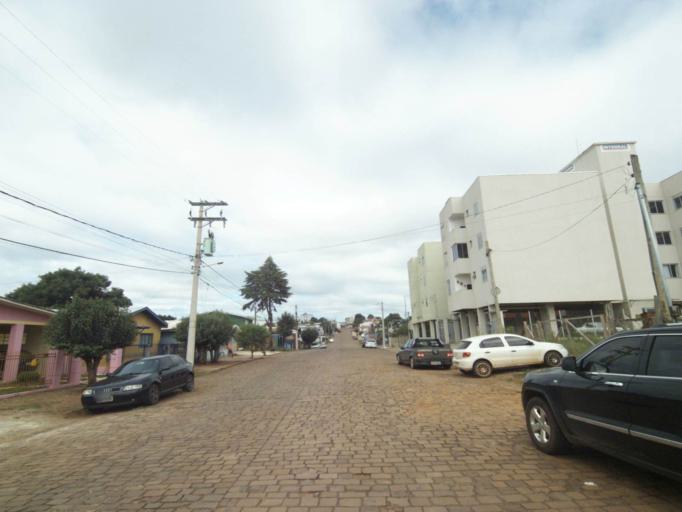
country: BR
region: Rio Grande do Sul
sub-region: Lagoa Vermelha
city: Lagoa Vermelha
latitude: -28.2110
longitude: -51.5123
